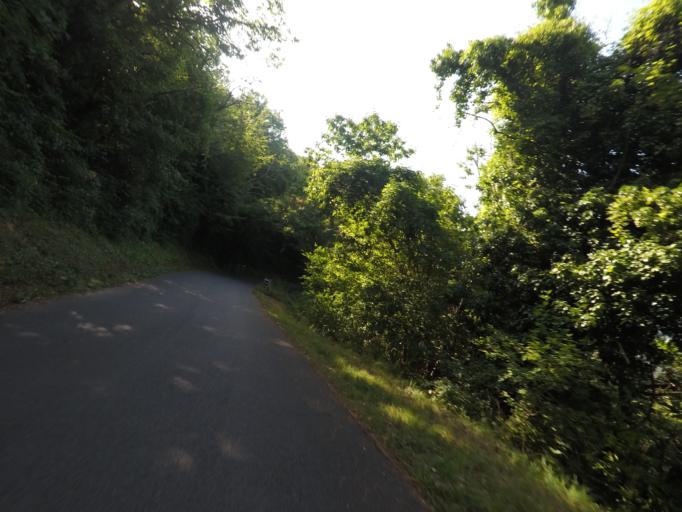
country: IT
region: Liguria
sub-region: Provincia di La Spezia
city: Casano-Dogana-Isola
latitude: 44.0876
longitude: 10.0592
